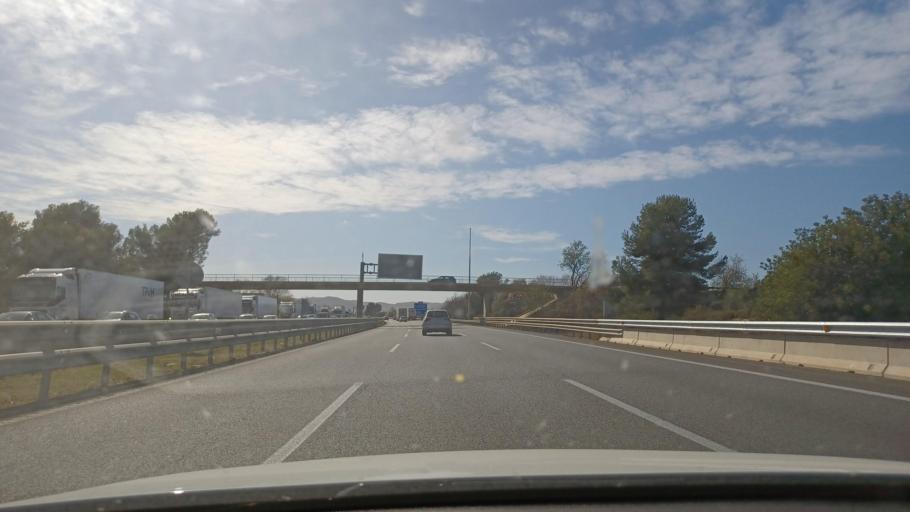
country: ES
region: Catalonia
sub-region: Provincia de Tarragona
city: Sant Jaume dels Domenys
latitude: 41.2792
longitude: 1.5644
